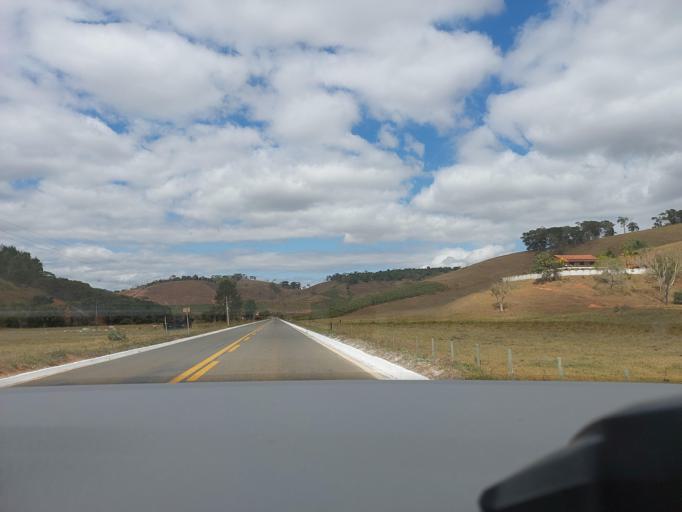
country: BR
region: Minas Gerais
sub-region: Vicosa
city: Vicosa
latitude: -20.8444
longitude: -42.6757
